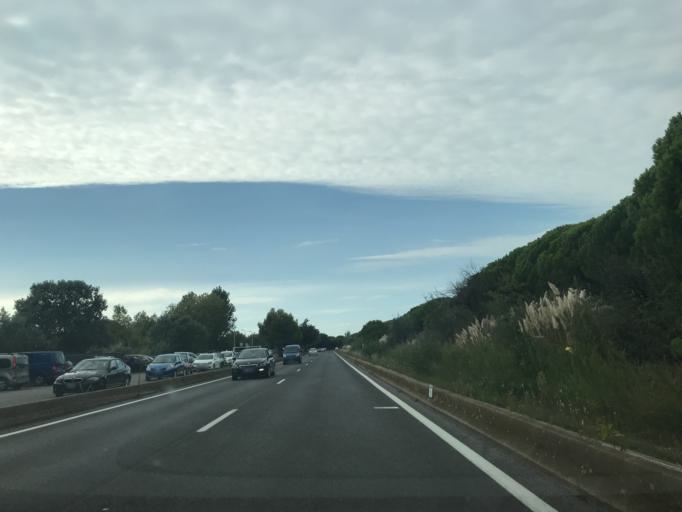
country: FR
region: Languedoc-Roussillon
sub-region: Departement du Gard
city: Le Grau-du-Roi
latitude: 43.5524
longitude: 4.1143
